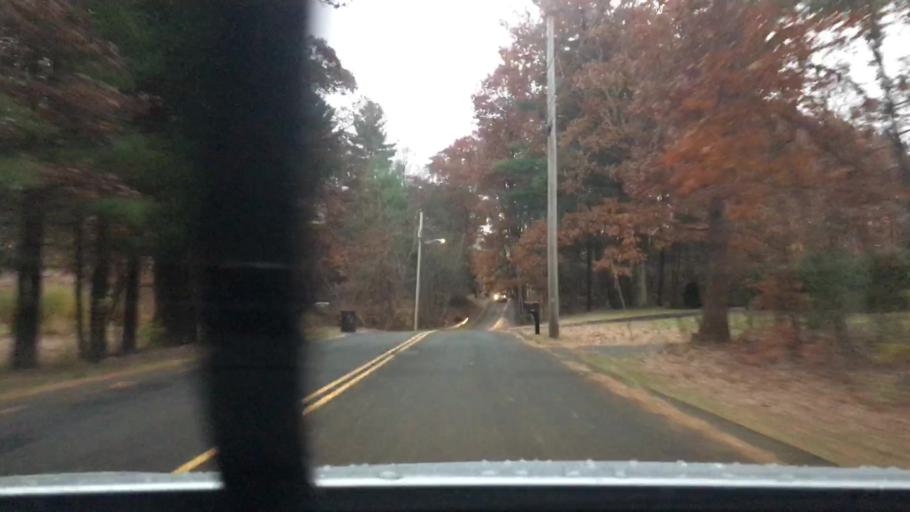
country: US
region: Massachusetts
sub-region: Hampden County
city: Westfield
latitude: 42.1039
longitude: -72.7810
